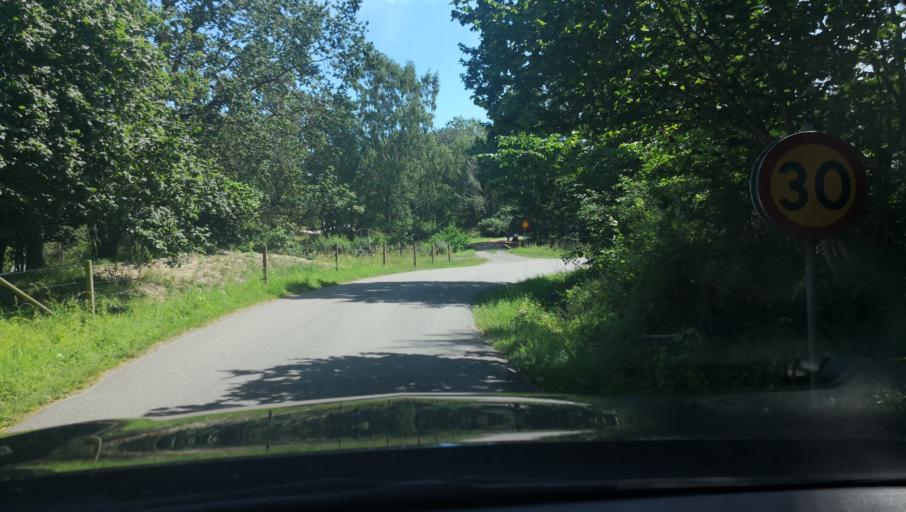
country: SE
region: Skane
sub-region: Ystads Kommun
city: Kopingebro
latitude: 55.3875
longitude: 14.1460
